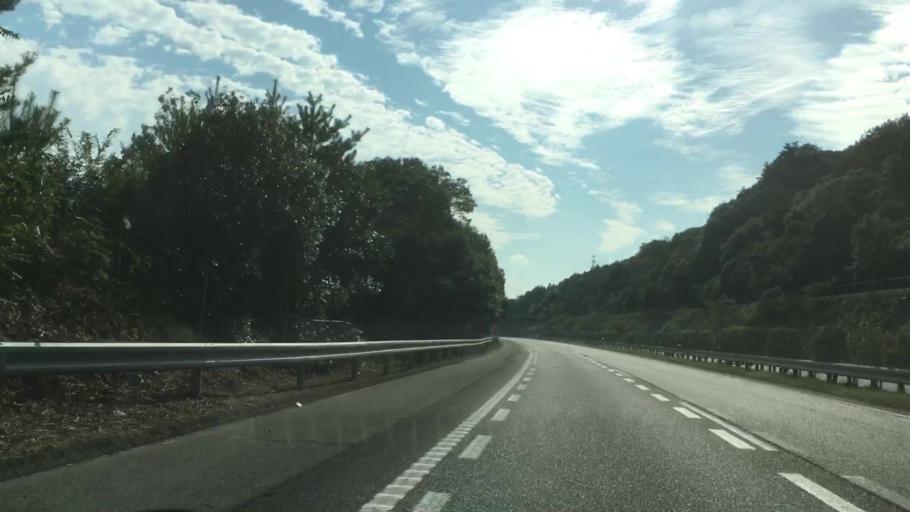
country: JP
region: Yamaguchi
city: Hikari
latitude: 34.0570
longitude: 132.0060
